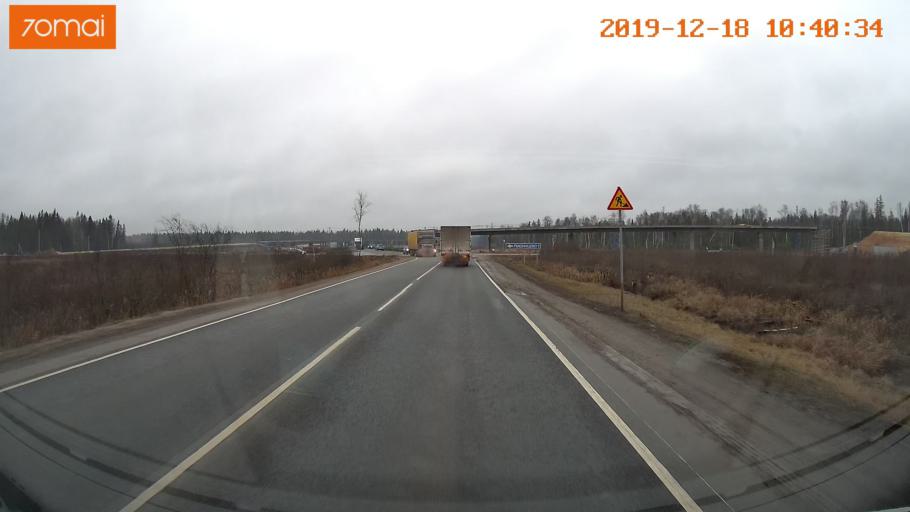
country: RU
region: Moskovskaya
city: Aprelevka
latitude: 55.4517
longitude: 37.1214
